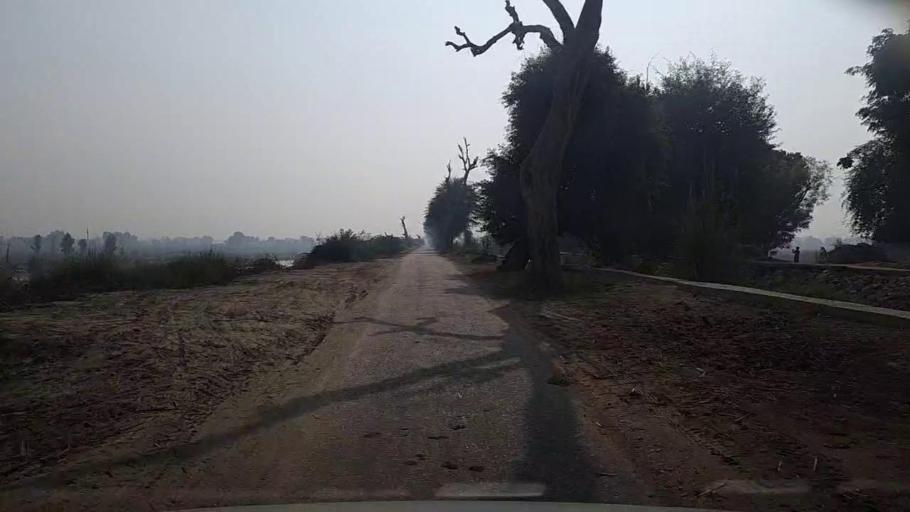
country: PK
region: Sindh
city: Setharja Old
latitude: 27.1095
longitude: 68.5086
